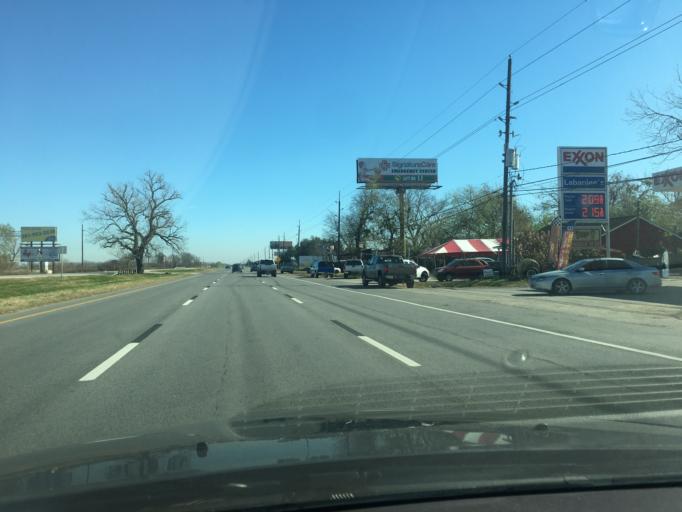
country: US
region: Texas
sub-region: Fort Bend County
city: Pecan Grove
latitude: 29.5964
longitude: -95.7336
